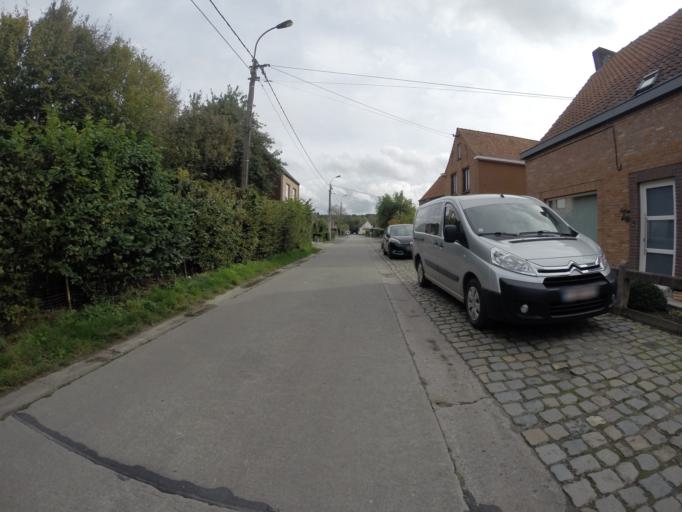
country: BE
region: Flanders
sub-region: Provincie West-Vlaanderen
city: Beernem
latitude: 51.0933
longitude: 3.3700
